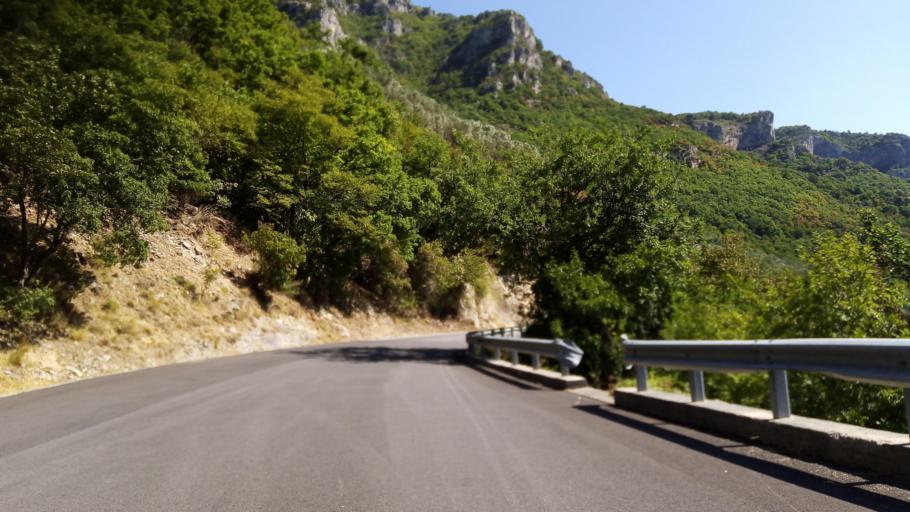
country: IT
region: Liguria
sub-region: Provincia di Savona
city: Balestrino
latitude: 44.1387
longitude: 8.1867
